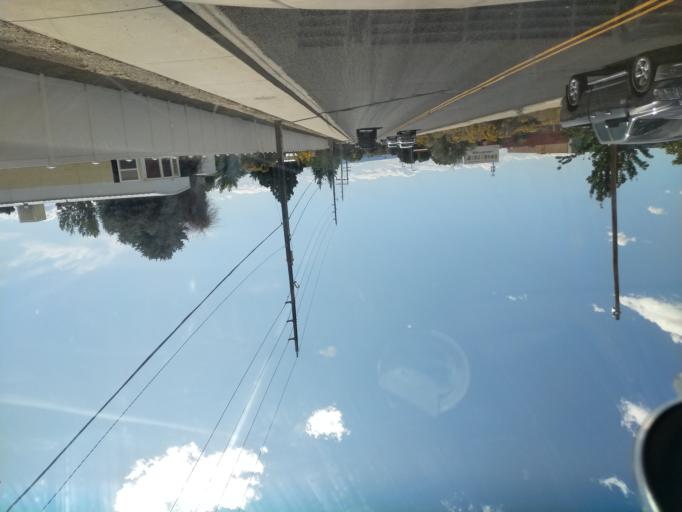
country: US
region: Colorado
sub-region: Mesa County
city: Clifton
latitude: 39.0911
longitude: -108.4595
